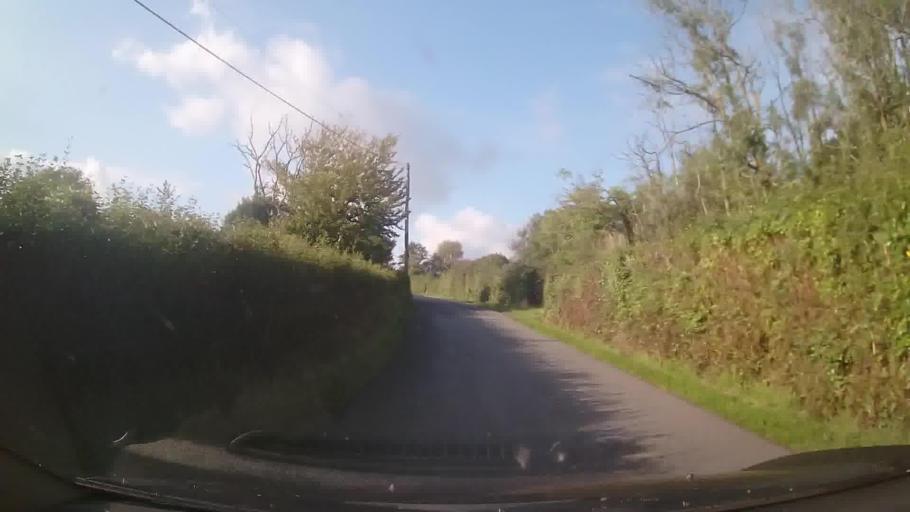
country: GB
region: Wales
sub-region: Pembrokeshire
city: Saundersfoot
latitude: 51.7545
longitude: -4.6504
